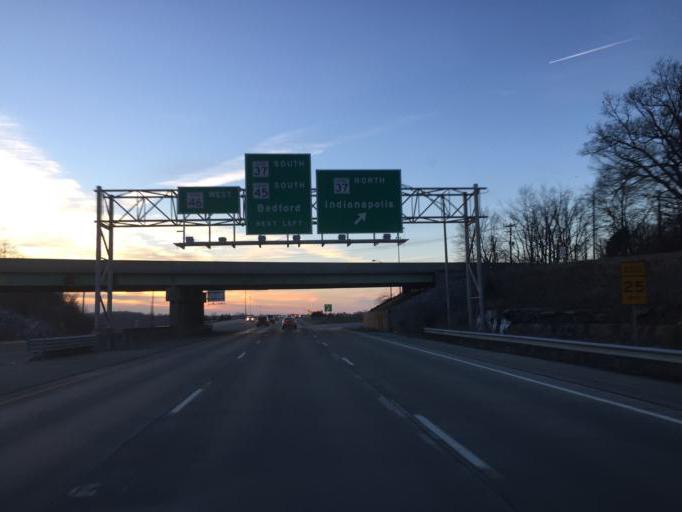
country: US
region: Indiana
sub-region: Monroe County
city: Bloomington
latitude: 39.1871
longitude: -86.5506
